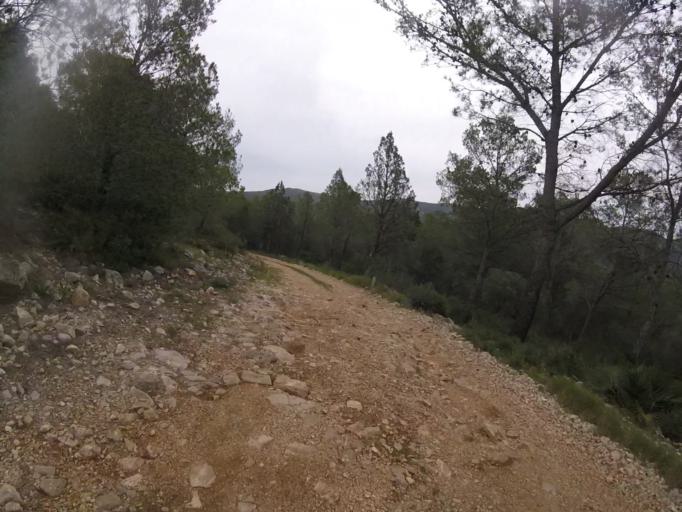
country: ES
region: Valencia
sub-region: Provincia de Castello
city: Santa Magdalena de Pulpis
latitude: 40.3174
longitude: 0.2792
